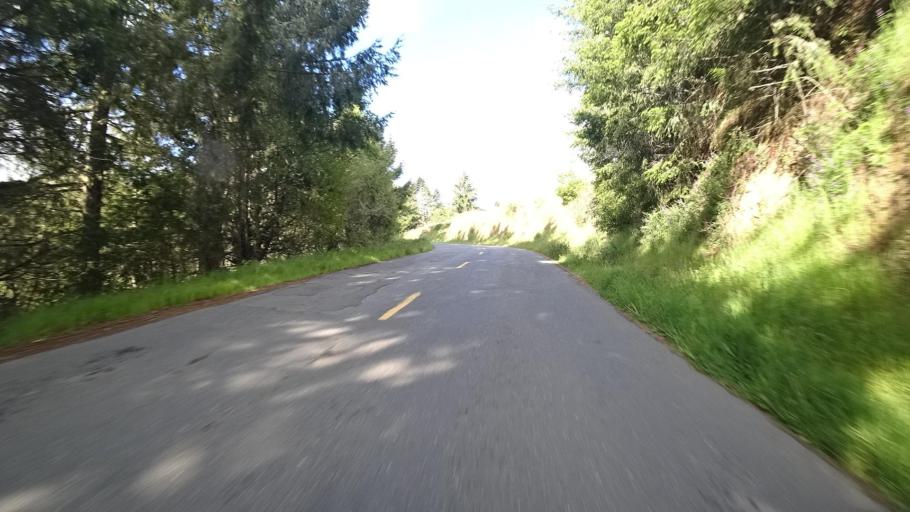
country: US
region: California
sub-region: Humboldt County
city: Ferndale
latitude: 40.5644
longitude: -124.2720
